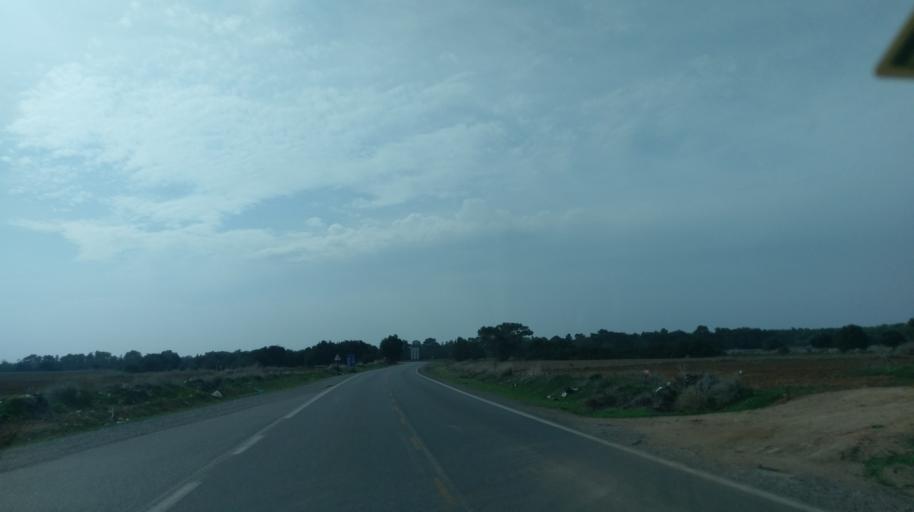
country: CY
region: Lefkosia
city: Morfou
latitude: 35.2960
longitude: 33.0439
